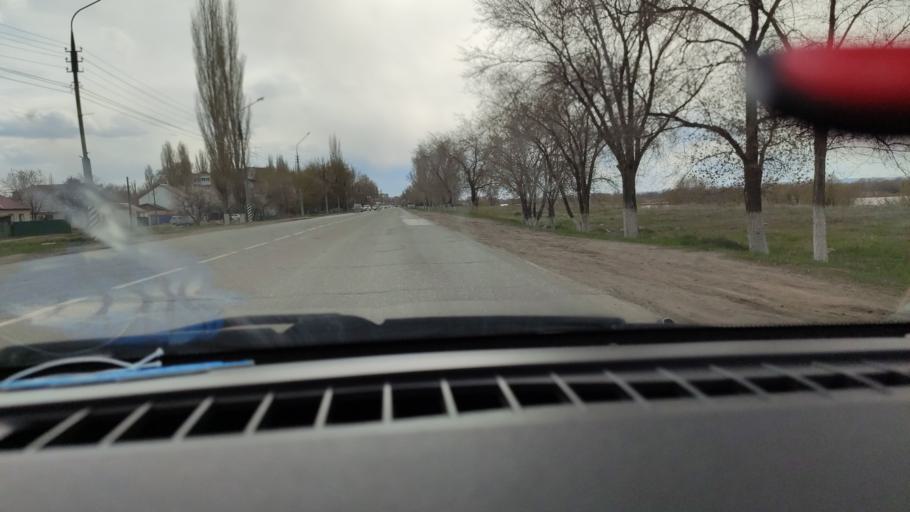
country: RU
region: Saratov
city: Engel's
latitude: 51.4561
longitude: 46.0871
